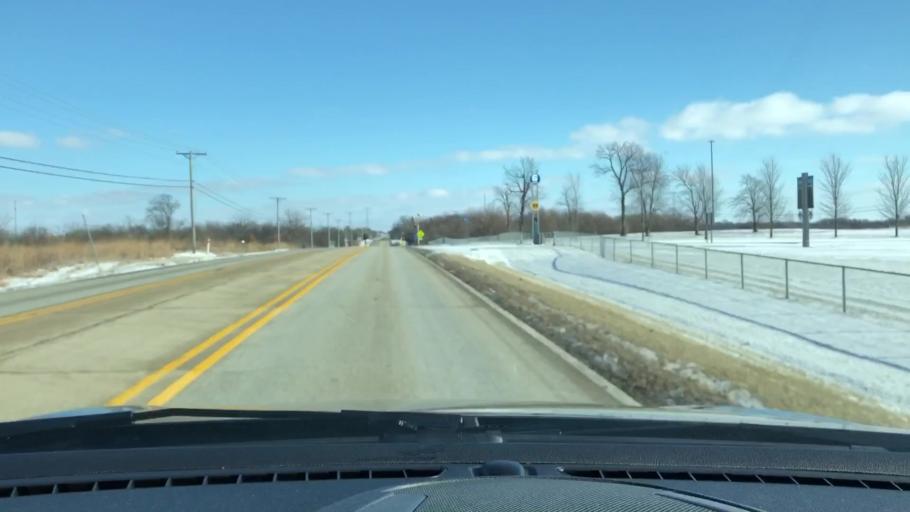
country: US
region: Illinois
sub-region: Will County
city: Preston Heights
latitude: 41.4815
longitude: -88.0458
